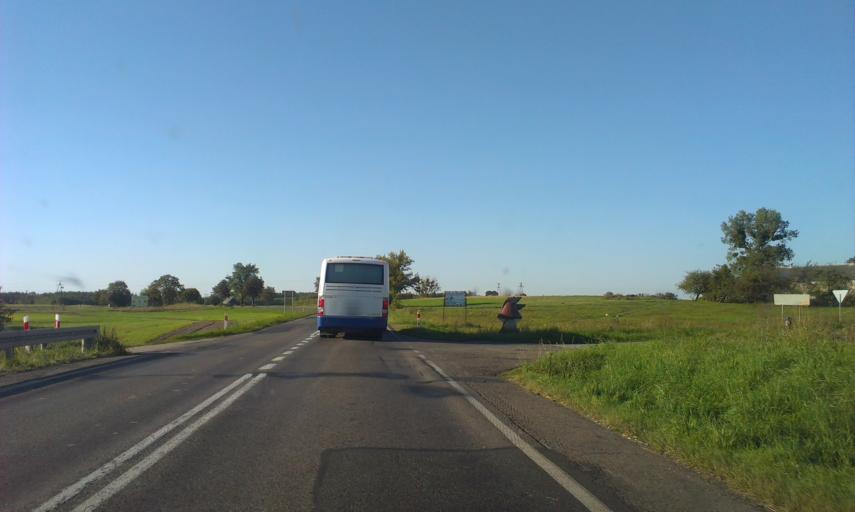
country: PL
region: Kujawsko-Pomorskie
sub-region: Powiat tucholski
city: Lubiewo
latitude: 53.5098
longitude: 17.9755
